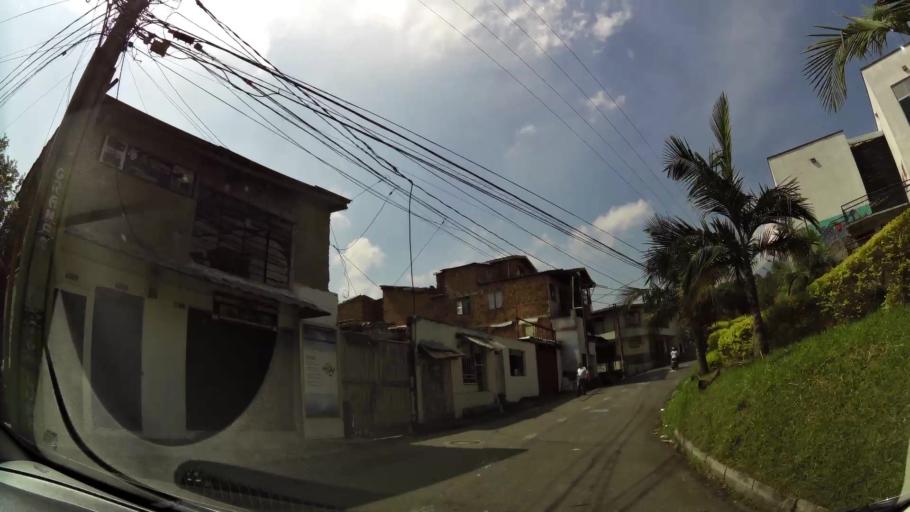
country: CO
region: Antioquia
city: La Estrella
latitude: 6.1836
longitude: -75.6411
